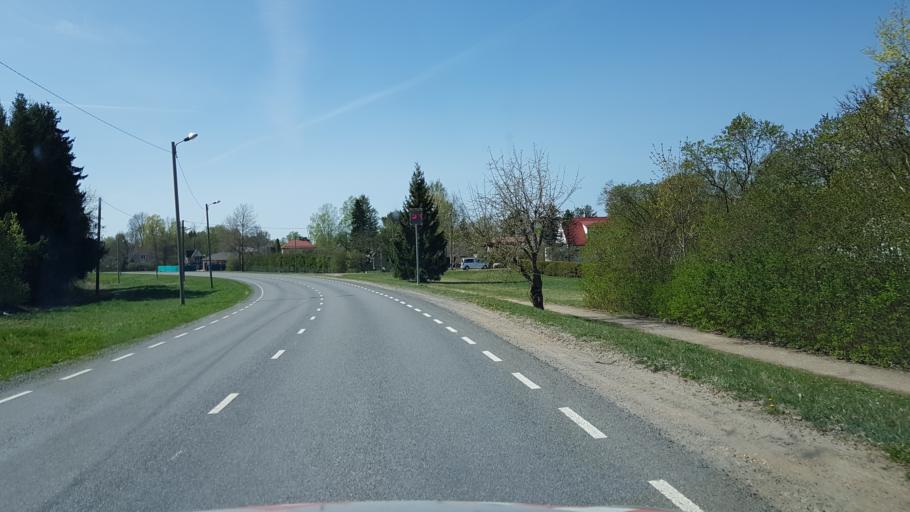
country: EE
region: Tartu
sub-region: Noo vald
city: Noo
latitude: 58.2816
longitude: 26.5485
